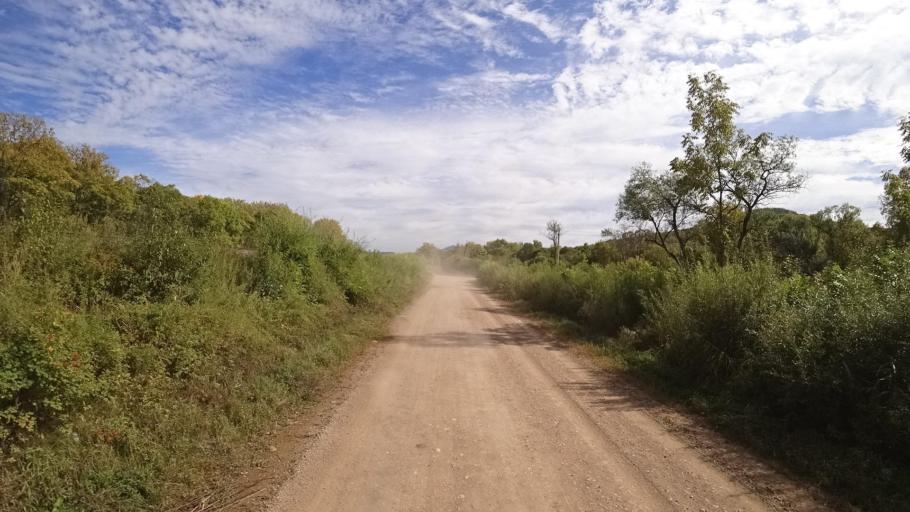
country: RU
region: Primorskiy
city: Yakovlevka
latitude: 44.3918
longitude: 133.6086
